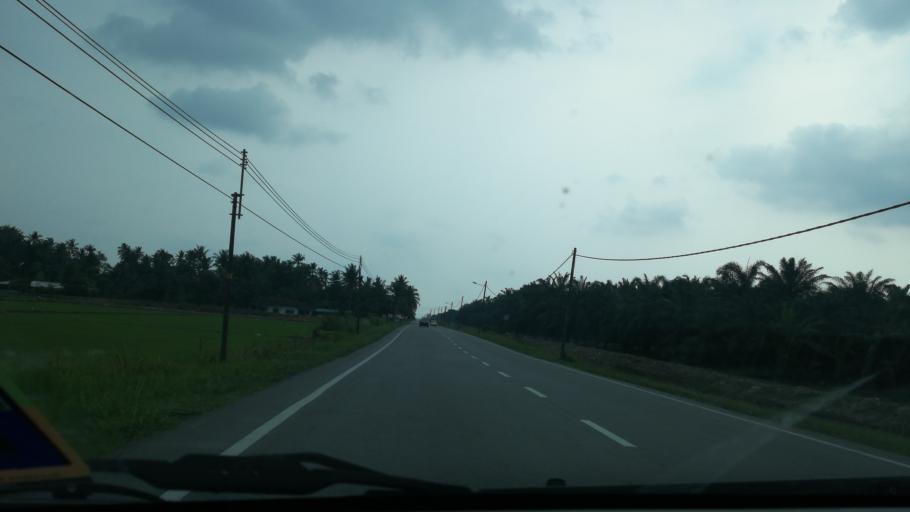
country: MY
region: Perak
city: Teluk Intan
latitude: 4.1163
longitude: 101.0733
